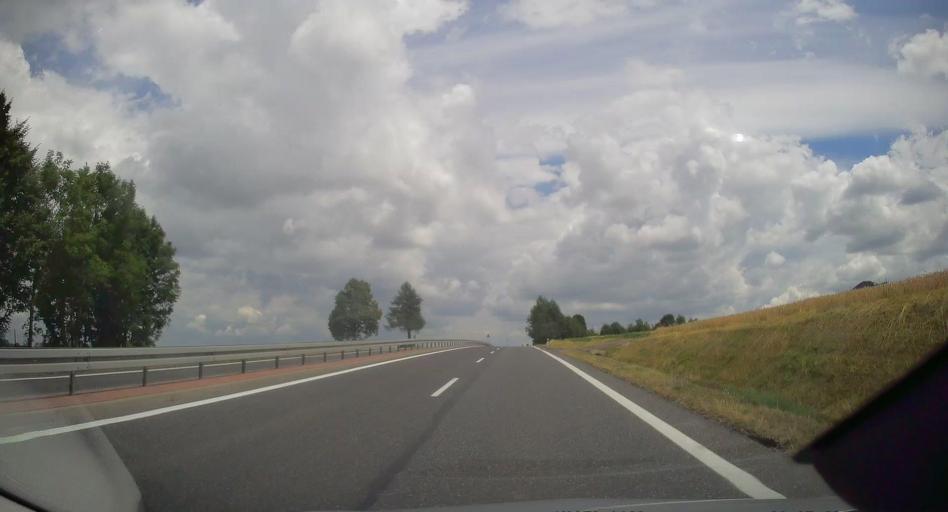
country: PL
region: Subcarpathian Voivodeship
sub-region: Powiat ropczycko-sedziszowski
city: Ostrow
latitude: 50.0619
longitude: 21.5534
